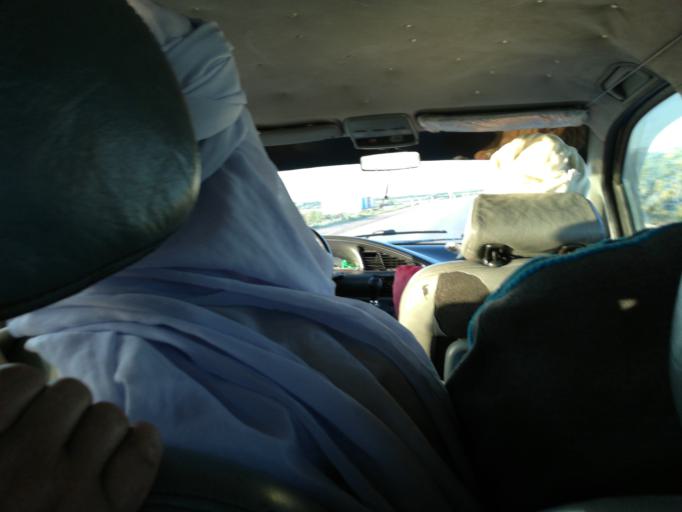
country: TN
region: Susah
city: Sidi Bou Ali
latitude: 36.0460
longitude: 10.3304
